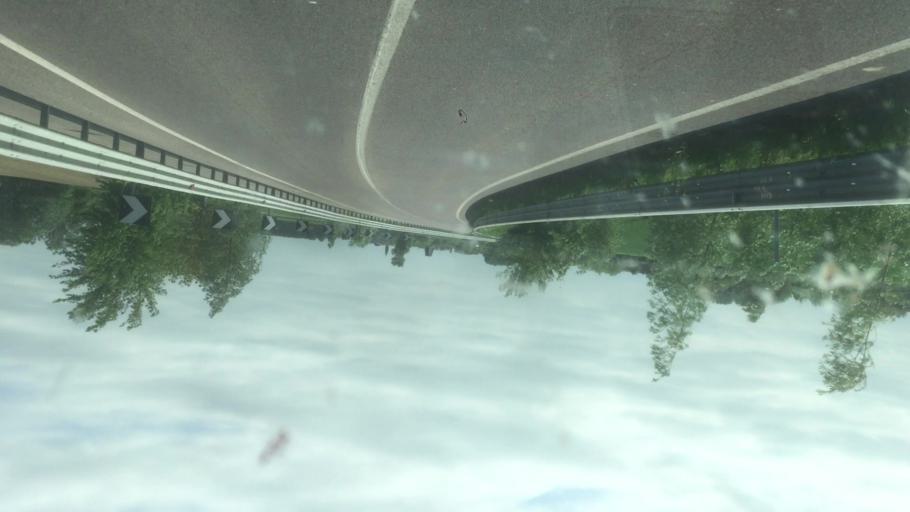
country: IT
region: Veneto
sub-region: Provincia di Rovigo
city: Calto
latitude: 45.0009
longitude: 11.3629
